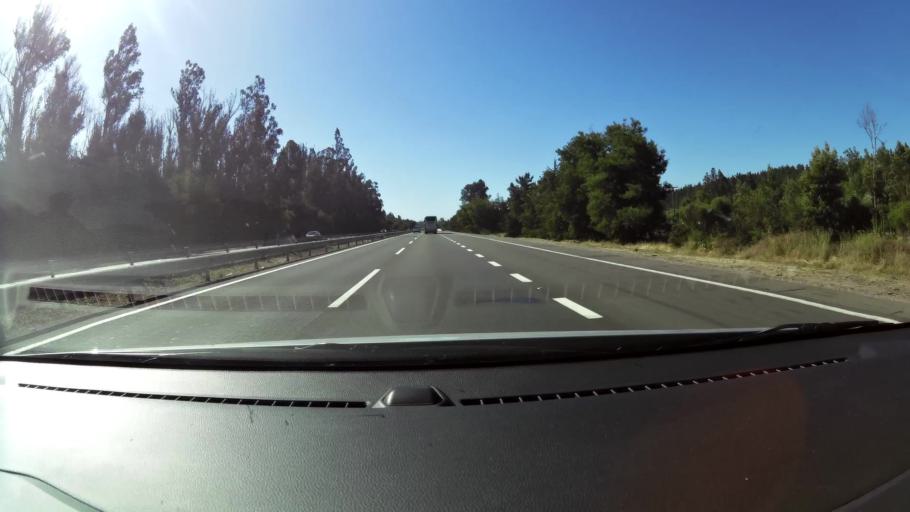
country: CL
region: Valparaiso
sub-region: Provincia de Marga Marga
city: Quilpue
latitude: -33.1905
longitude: -71.4977
